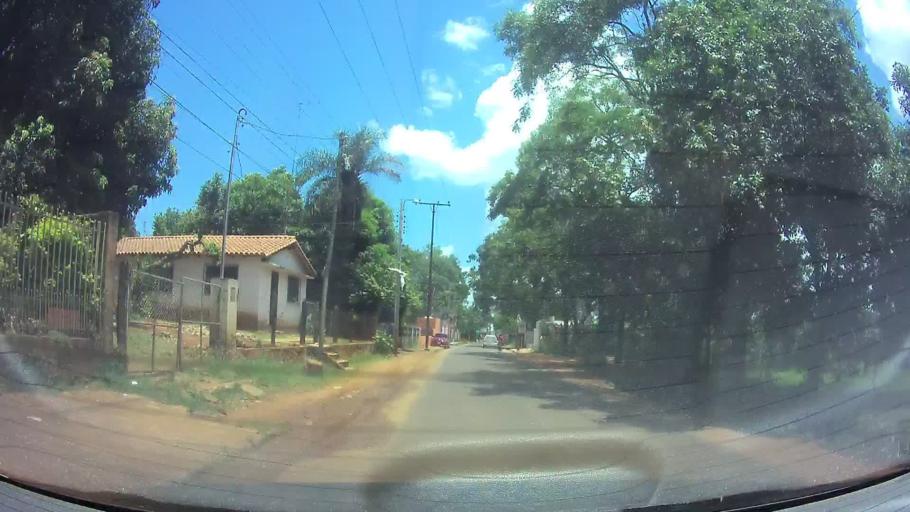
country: PY
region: Central
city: Itaugua
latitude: -25.3855
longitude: -57.3654
